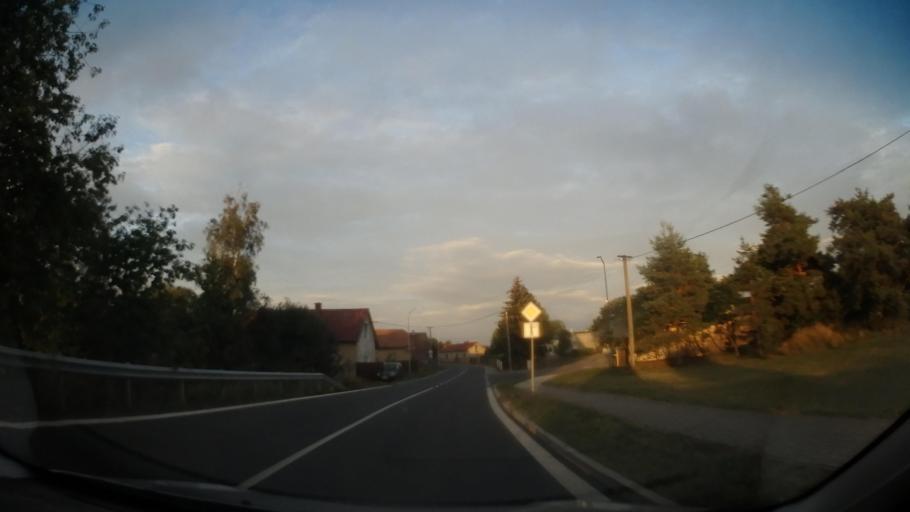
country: CZ
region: Central Bohemia
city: Milovice
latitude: 50.2317
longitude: 14.9539
